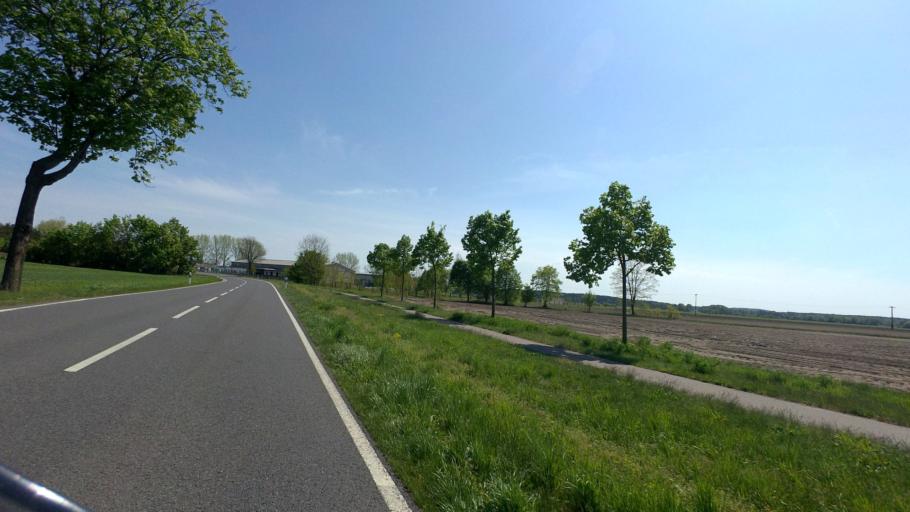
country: DE
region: Brandenburg
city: Schlepzig
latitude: 52.0537
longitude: 13.9791
